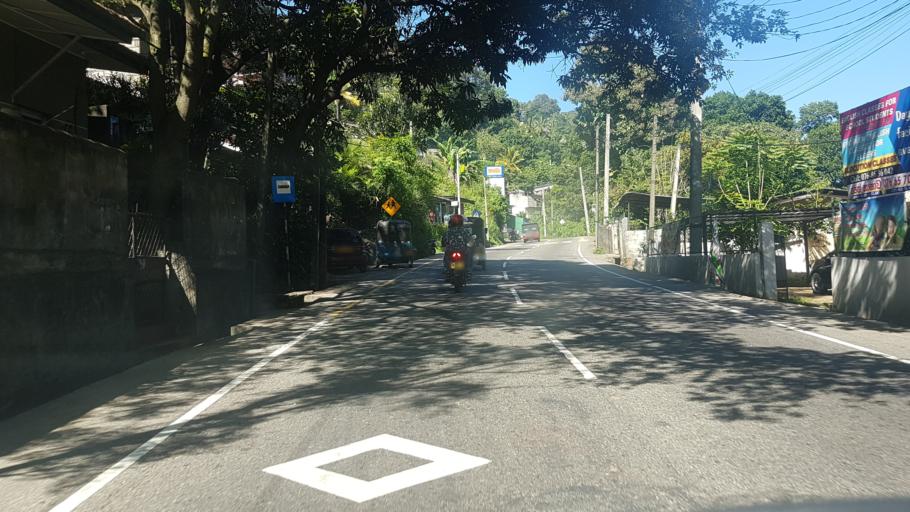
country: LK
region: Central
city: Kandy
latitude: 7.2866
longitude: 80.6598
